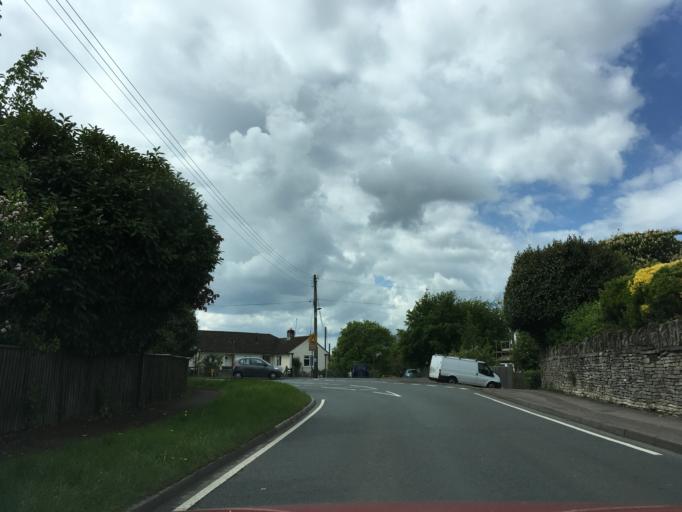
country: GB
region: England
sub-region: Gloucestershire
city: Stonehouse
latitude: 51.7347
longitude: -2.2752
